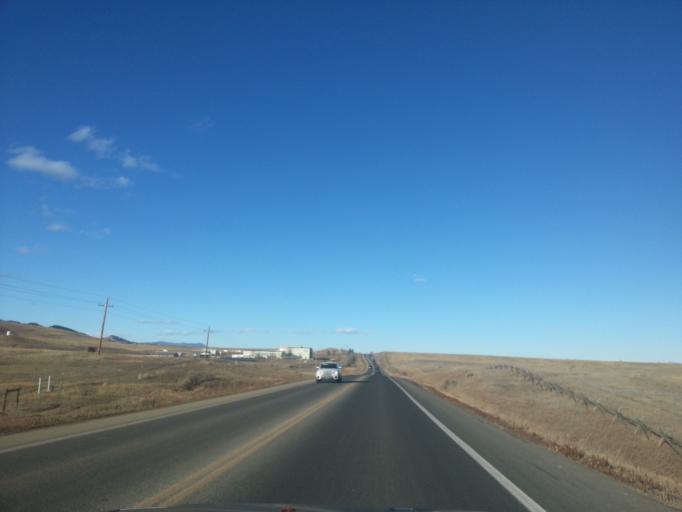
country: US
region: Colorado
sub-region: Larimer County
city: Fort Collins
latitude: 40.4982
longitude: -105.1154
